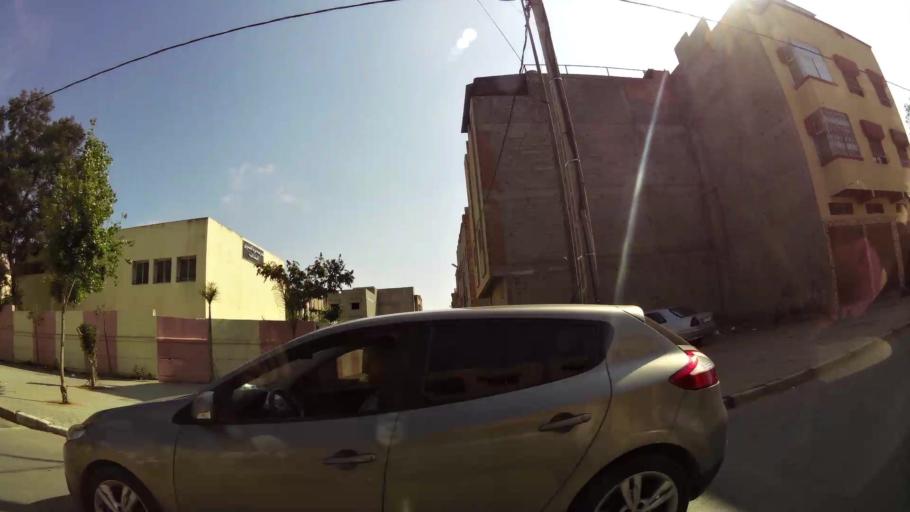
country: MA
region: Rabat-Sale-Zemmour-Zaer
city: Sale
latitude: 34.0596
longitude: -6.7703
